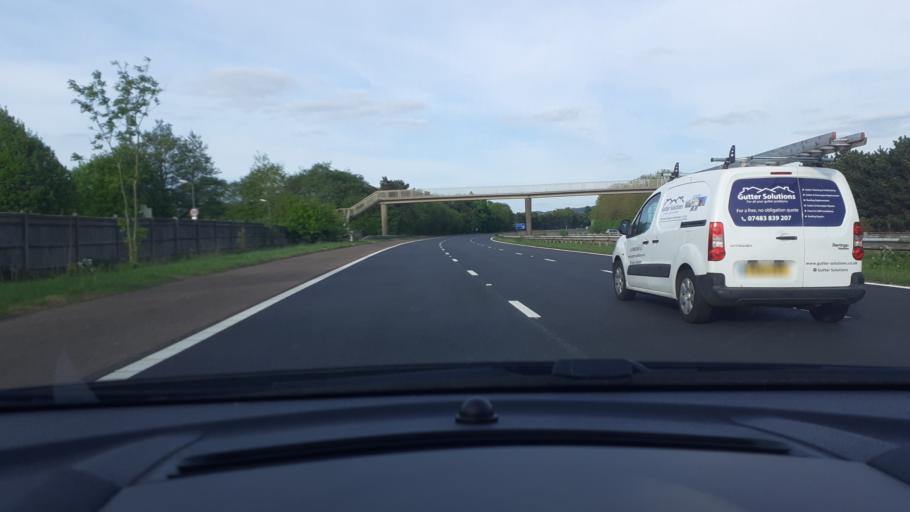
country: GB
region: England
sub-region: Lancashire
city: Skelmersdale
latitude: 53.5423
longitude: -2.8092
